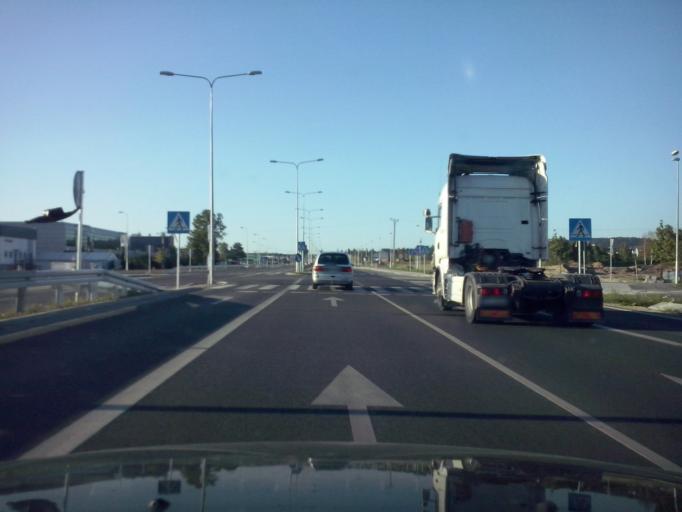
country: PL
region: Swietokrzyskie
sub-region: Powiat kielecki
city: Brzeziny
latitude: 50.8078
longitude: 20.6214
